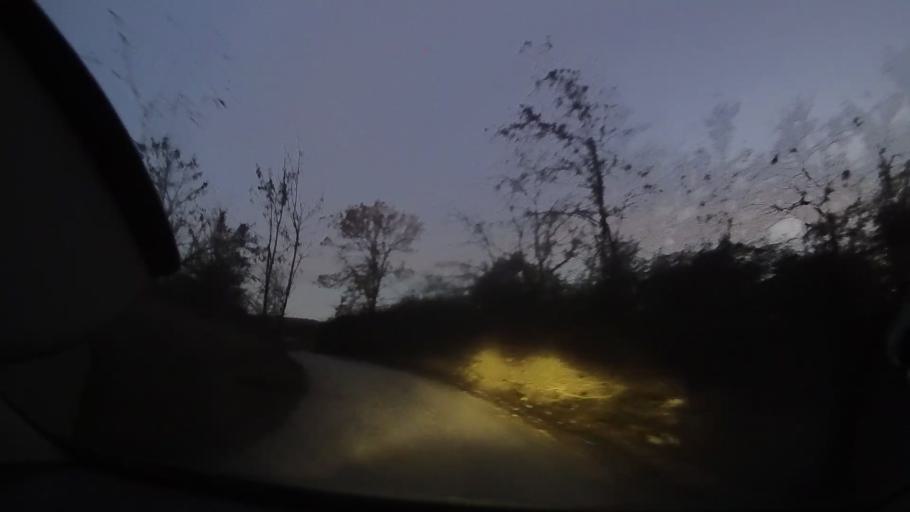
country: RO
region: Bihor
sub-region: Comuna Tetchea
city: Hotar
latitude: 47.0035
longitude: 22.3093
